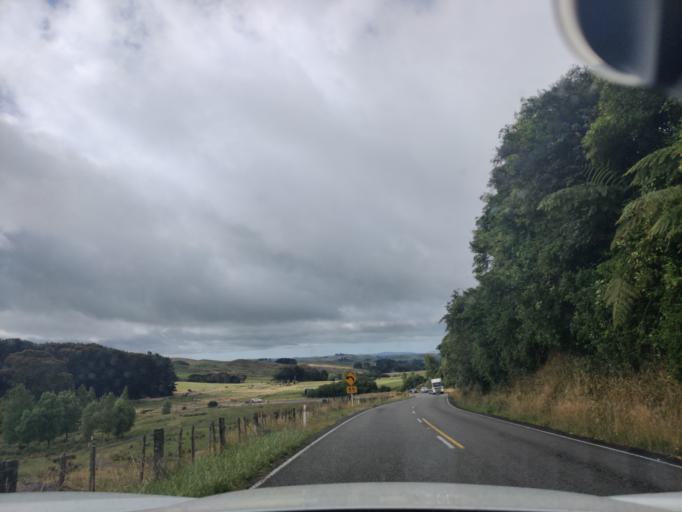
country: NZ
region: Manawatu-Wanganui
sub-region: Palmerston North City
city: Palmerston North
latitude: -40.4208
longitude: 175.7399
